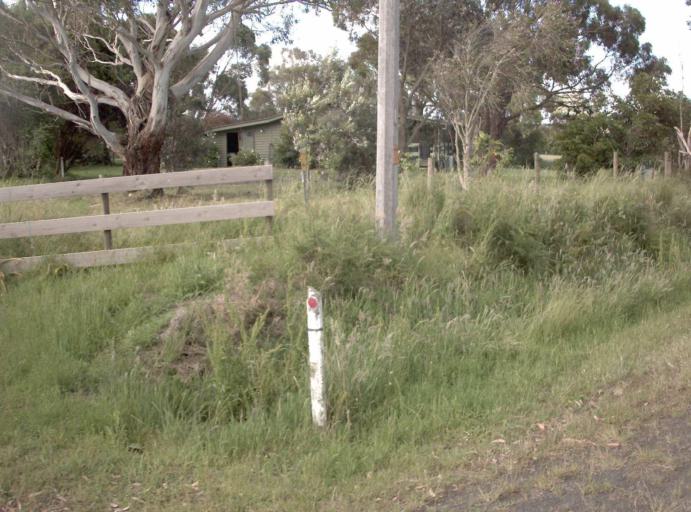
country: AU
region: Victoria
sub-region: Bass Coast
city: North Wonthaggi
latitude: -38.6082
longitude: 145.7588
